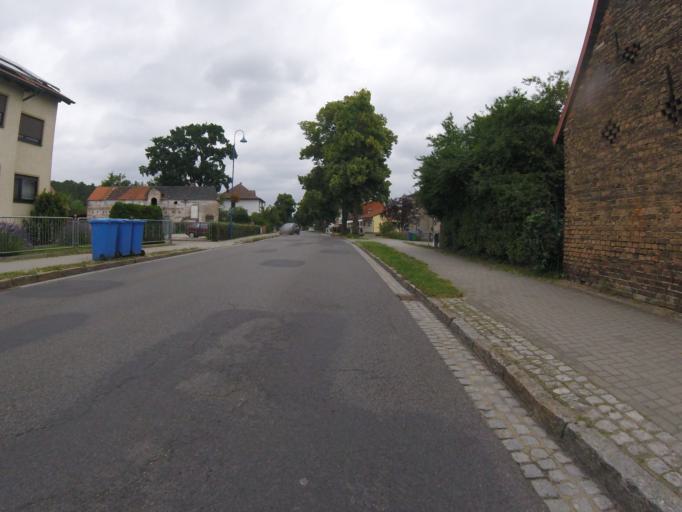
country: DE
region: Brandenburg
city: Bestensee
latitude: 52.2442
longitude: 13.6280
